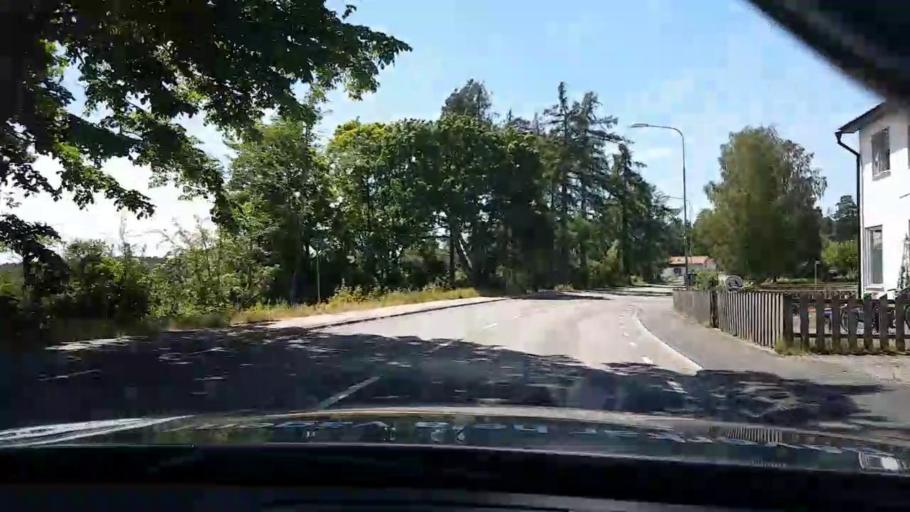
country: SE
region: Kalmar
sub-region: Vasterviks Kommun
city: Vaestervik
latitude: 57.9023
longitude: 16.6899
